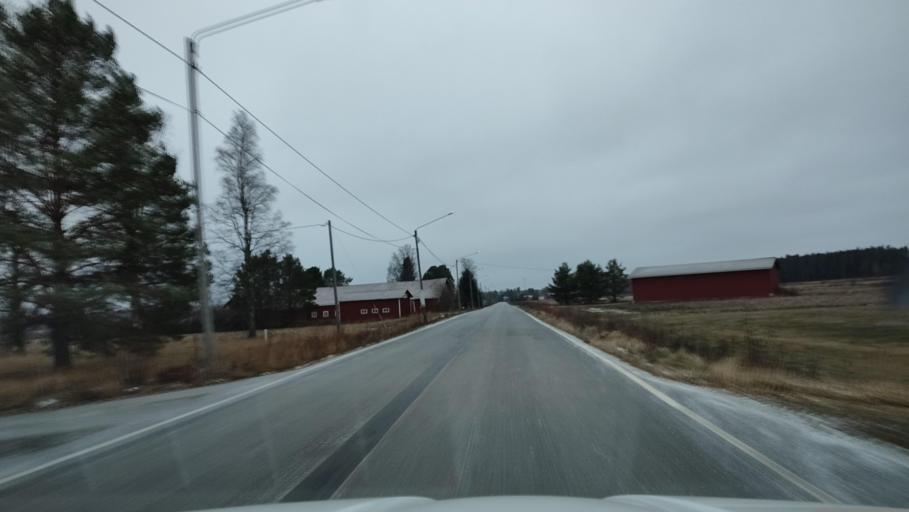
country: FI
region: Southern Ostrobothnia
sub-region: Suupohja
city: Karijoki
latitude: 62.2395
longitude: 21.6601
